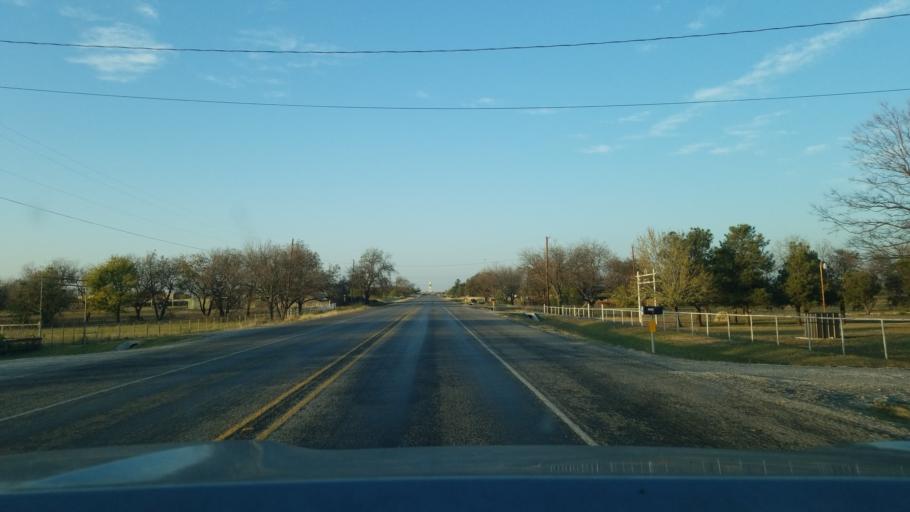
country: US
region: Texas
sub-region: Eastland County
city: Cisco
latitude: 32.3656
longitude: -98.9701
